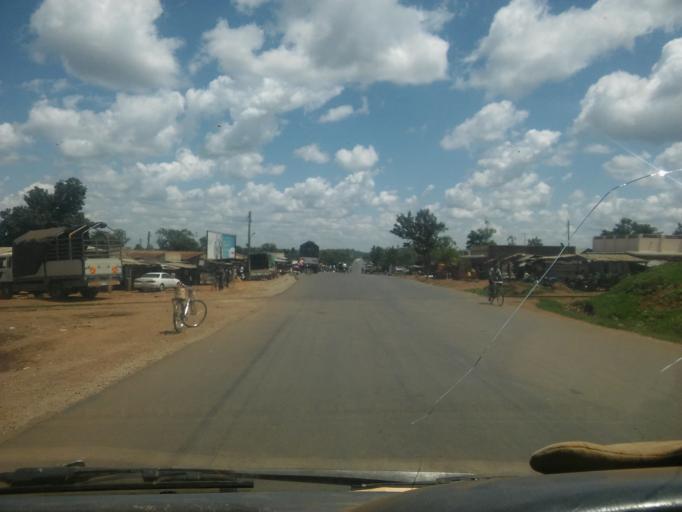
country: UG
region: Eastern Region
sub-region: Mbale District
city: Mbale
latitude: 1.0783
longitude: 34.1471
